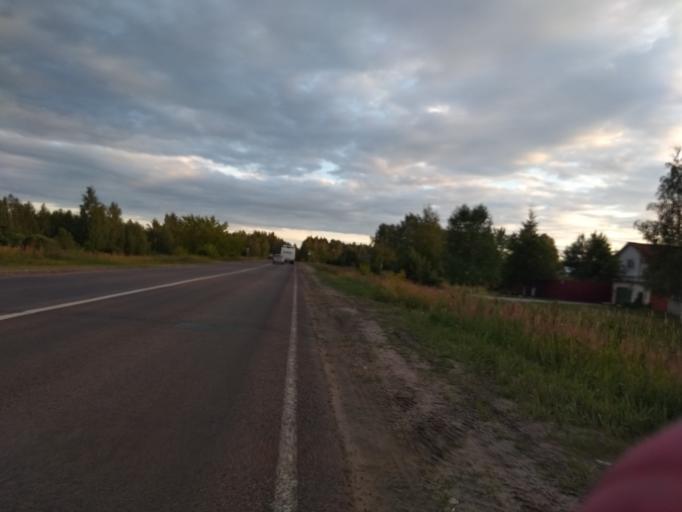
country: RU
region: Moskovskaya
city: Kerva
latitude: 55.5860
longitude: 39.6994
